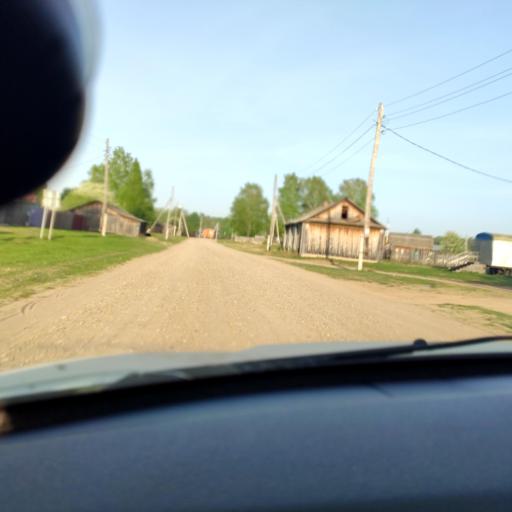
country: RU
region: Perm
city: Chermoz
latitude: 58.6000
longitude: 56.1015
